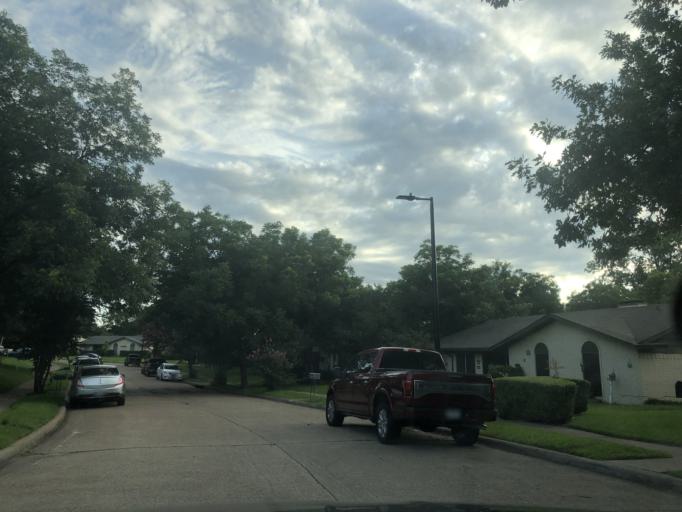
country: US
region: Texas
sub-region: Dallas County
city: Rowlett
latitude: 32.8512
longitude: -96.5900
